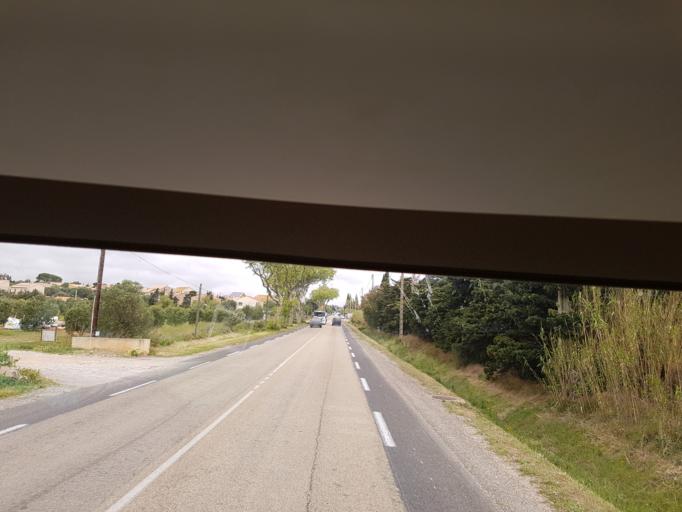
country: FR
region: Languedoc-Roussillon
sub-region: Departement de l'Aude
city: Leucate
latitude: 42.8909
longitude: 2.9958
